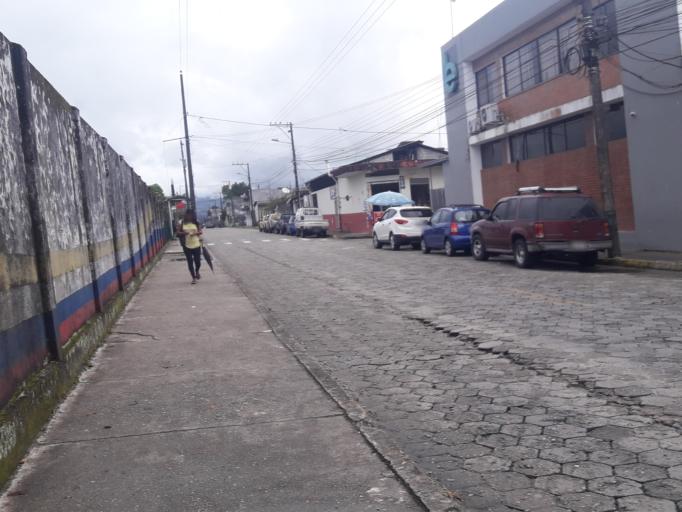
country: EC
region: Napo
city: Tena
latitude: -0.9879
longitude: -77.8179
